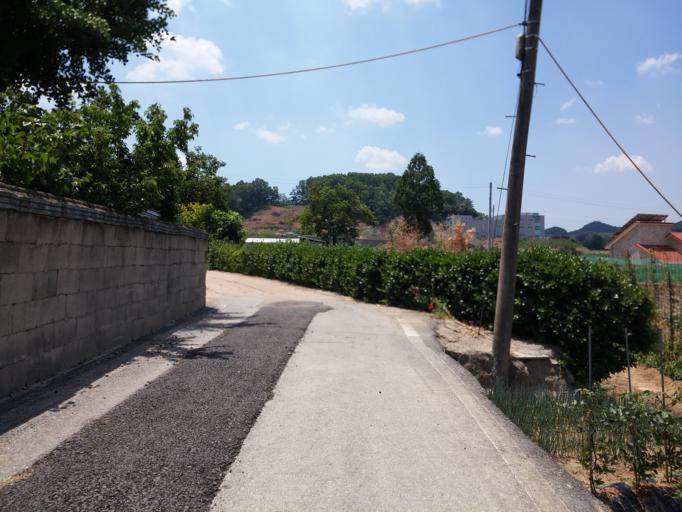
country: KR
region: Chungcheongbuk-do
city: Cheongju-si
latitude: 36.5553
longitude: 127.4359
